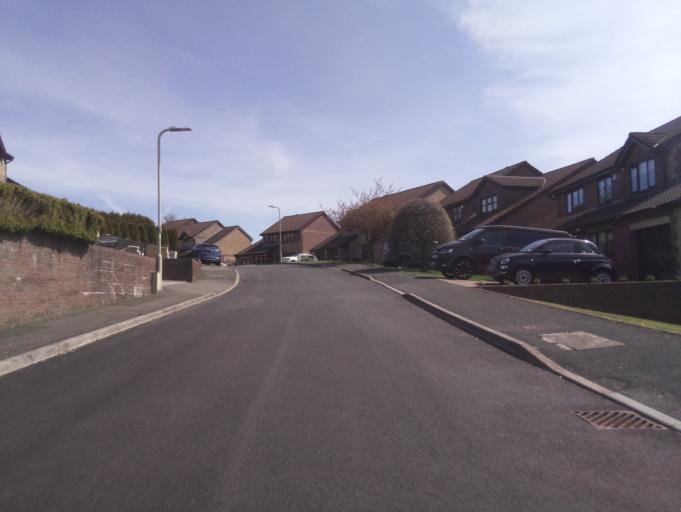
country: GB
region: Wales
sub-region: Merthyr Tydfil County Borough
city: Merthyr Tydfil
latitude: 51.7738
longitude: -3.3587
